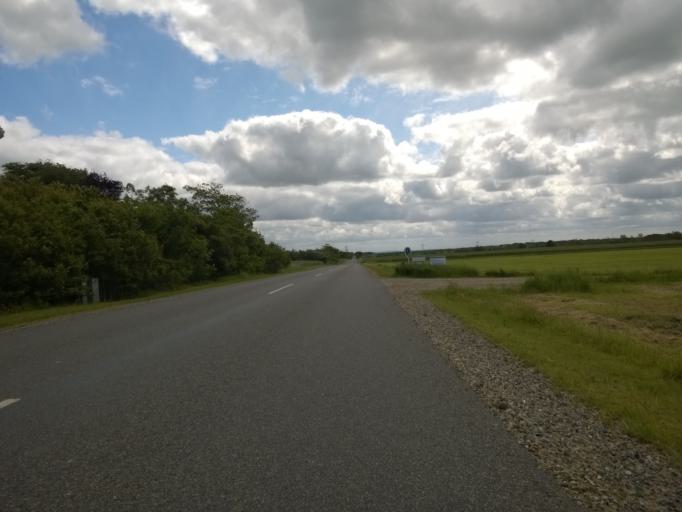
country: DK
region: Central Jutland
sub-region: Holstebro Kommune
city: Vinderup
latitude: 56.4218
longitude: 8.8438
